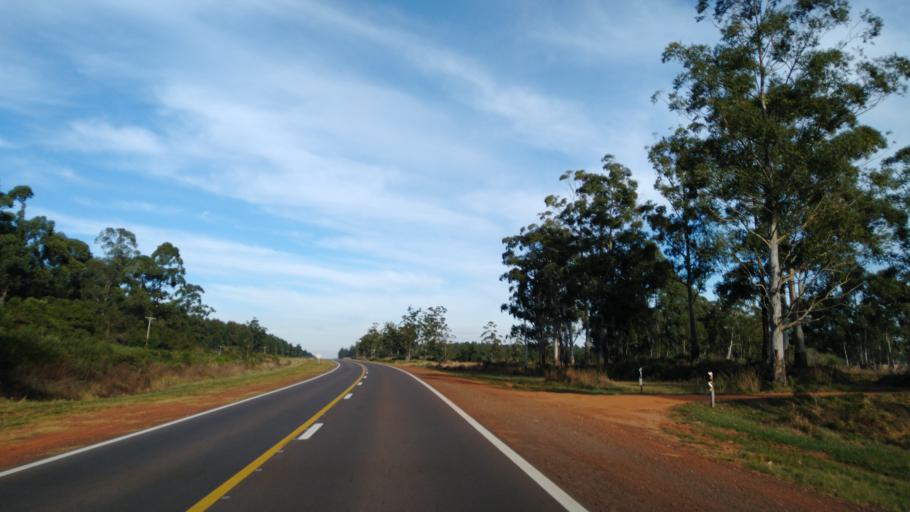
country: AR
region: Corrientes
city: Yapeyu
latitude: -29.4291
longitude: -56.8726
